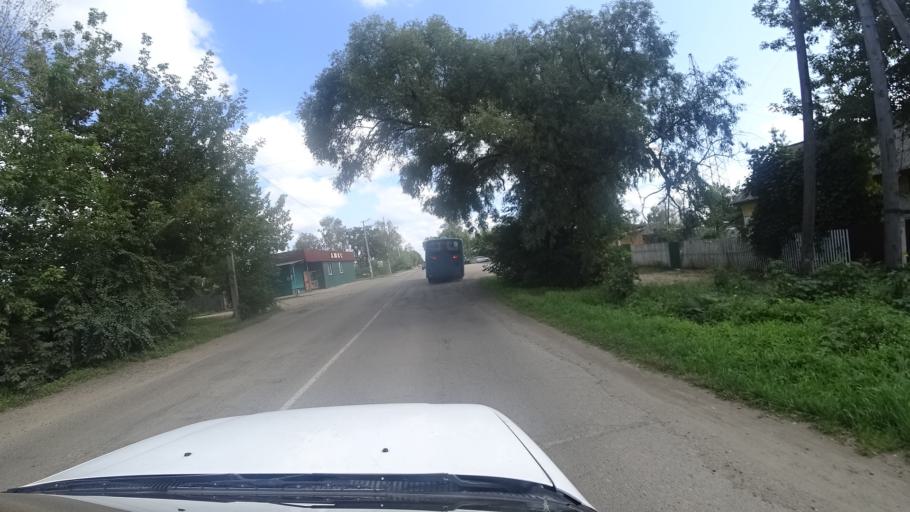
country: RU
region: Primorskiy
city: Dal'nerechensk
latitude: 45.9278
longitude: 133.7660
